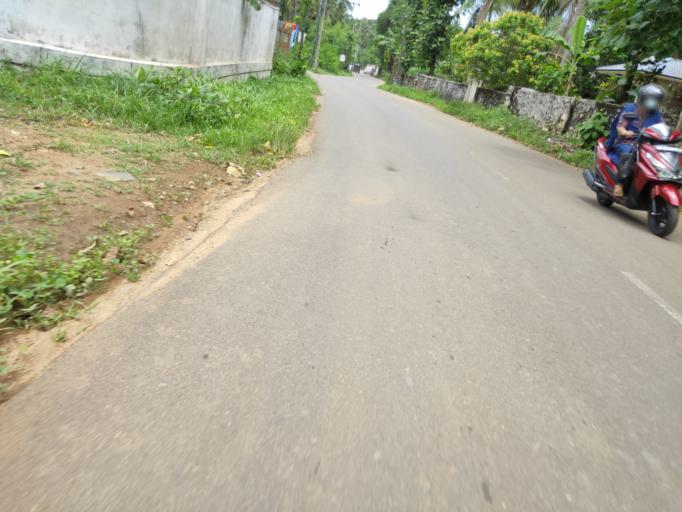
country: IN
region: Kerala
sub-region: Malappuram
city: Manjeri
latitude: 11.2054
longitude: 76.2595
